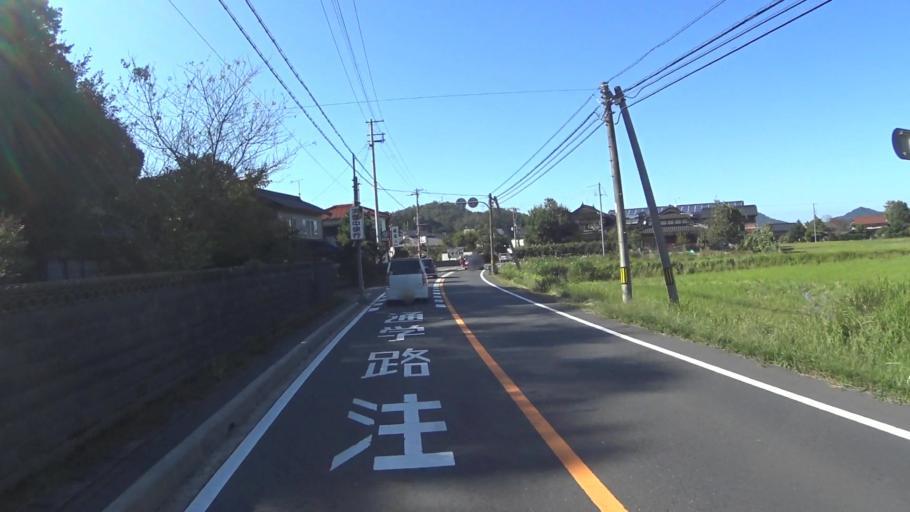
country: JP
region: Hyogo
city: Toyooka
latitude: 35.5810
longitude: 134.9645
